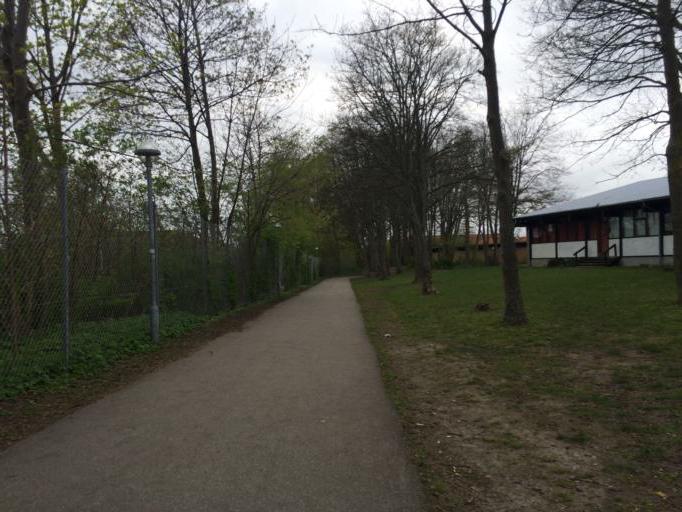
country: DK
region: Capital Region
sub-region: Vallensbaek Kommune
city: Vallensbaek
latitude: 55.6206
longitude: 12.3889
